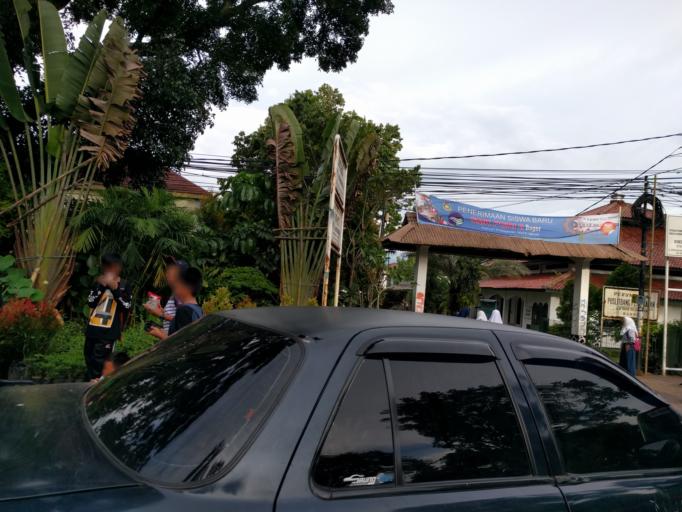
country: ID
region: West Java
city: Bogor
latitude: -6.5837
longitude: 106.8063
